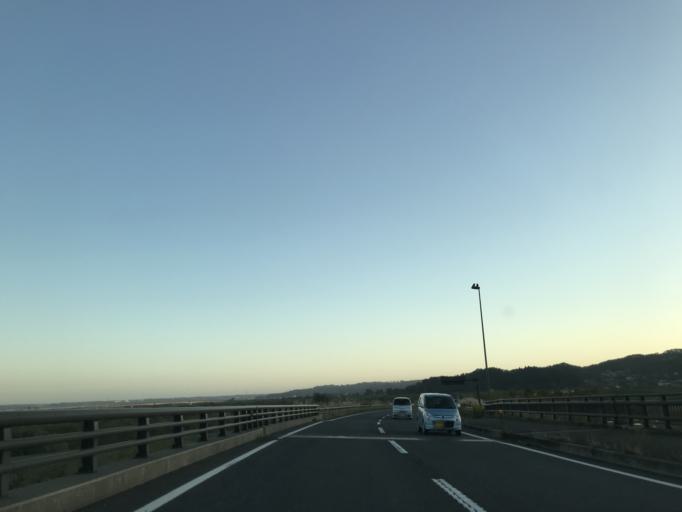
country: JP
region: Iwate
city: Ichinoseki
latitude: 39.0112
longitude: 141.1176
